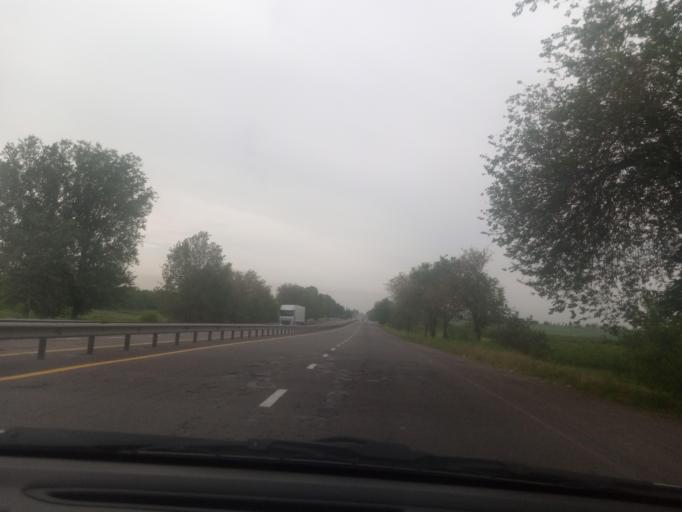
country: UZ
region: Toshkent
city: Tuytepa
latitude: 41.0940
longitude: 69.4604
